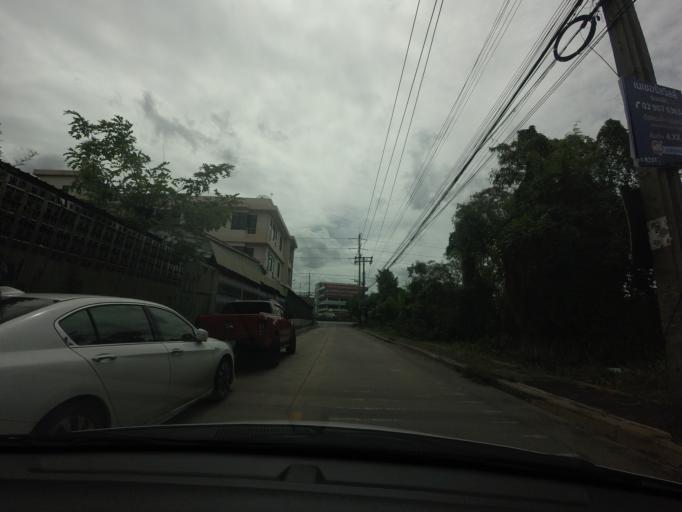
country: TH
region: Bangkok
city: Min Buri
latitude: 13.7922
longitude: 100.7468
